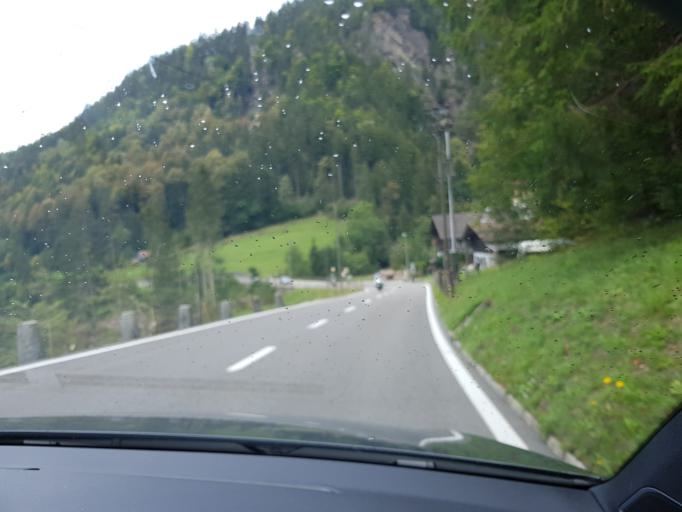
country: CH
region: Bern
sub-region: Interlaken-Oberhasli District
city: Meiringen
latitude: 46.7138
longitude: 8.2670
